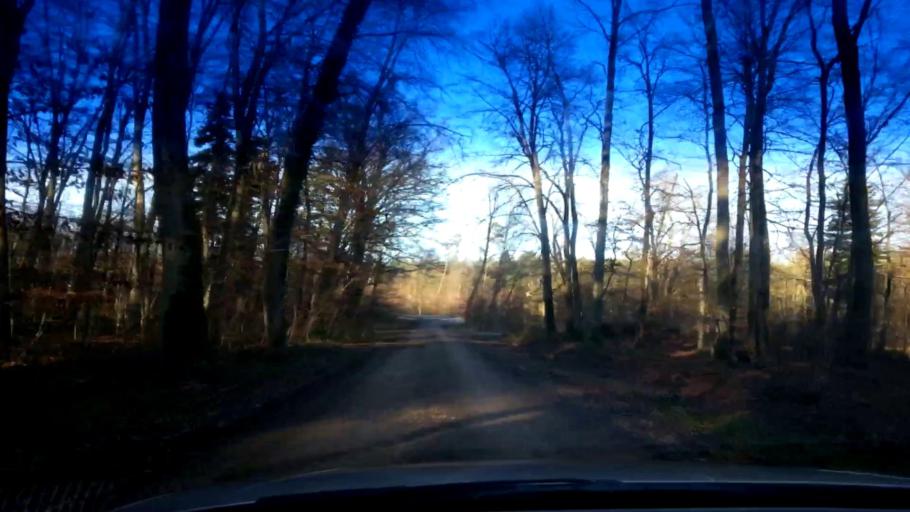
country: DE
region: Bavaria
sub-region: Upper Franconia
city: Memmelsdorf
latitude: 49.9032
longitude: 10.9585
